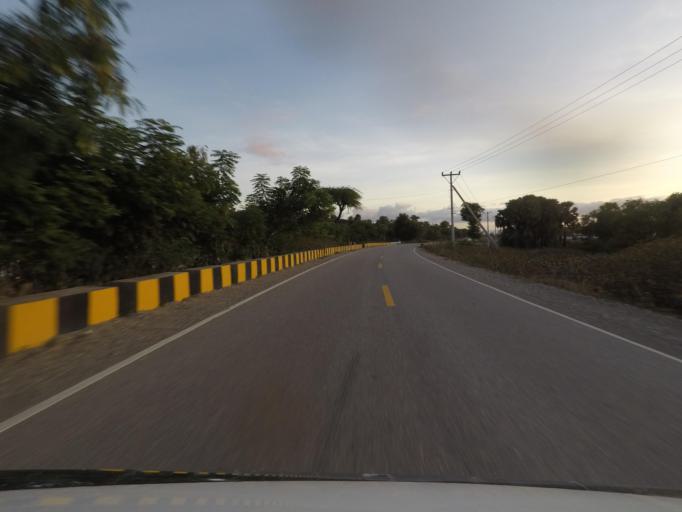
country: TL
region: Baucau
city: Baucau
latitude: -8.4615
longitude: 126.6105
